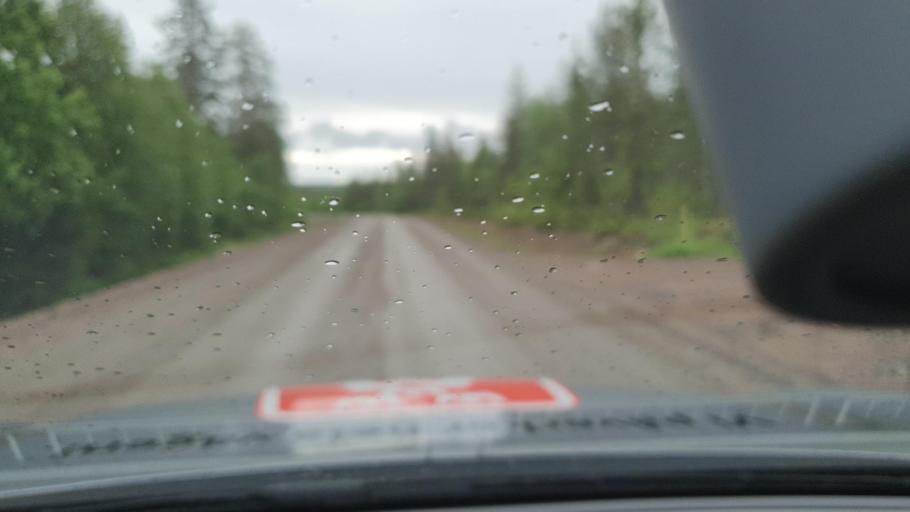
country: SE
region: Norrbotten
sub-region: Overtornea Kommun
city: OEvertornea
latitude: 66.4352
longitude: 23.5114
